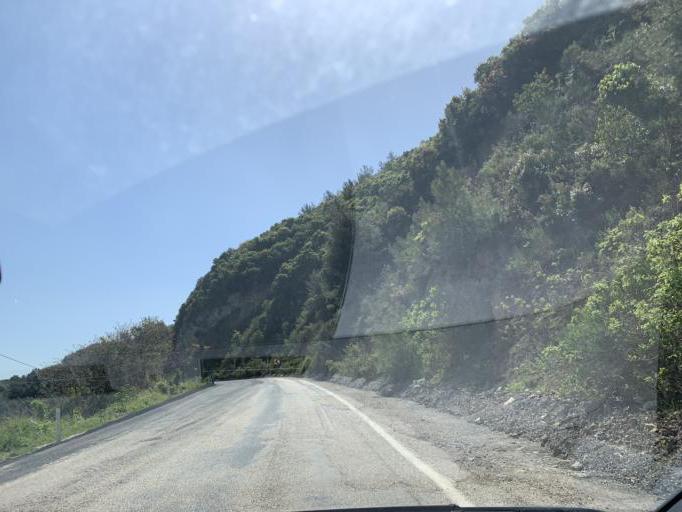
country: TR
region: Bursa
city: Niluefer
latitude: 40.3555
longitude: 28.9756
